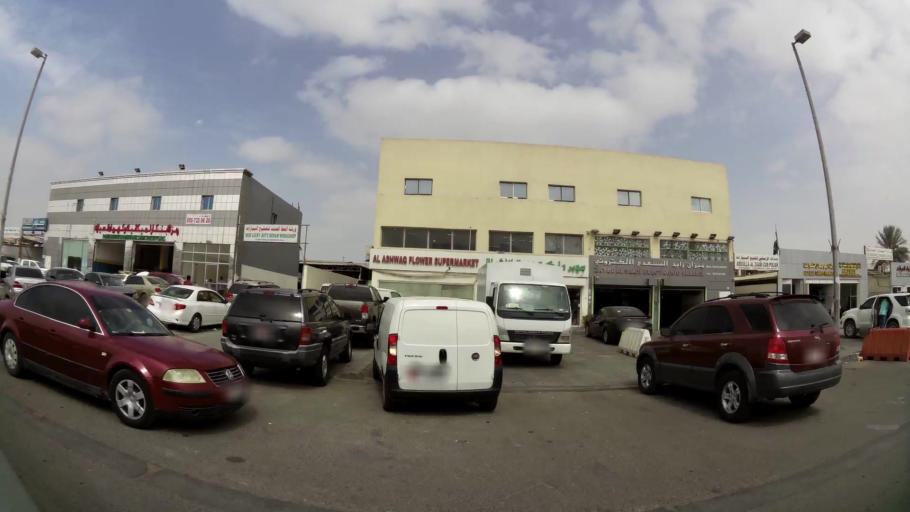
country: AE
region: Abu Dhabi
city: Abu Dhabi
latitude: 24.3811
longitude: 54.5131
